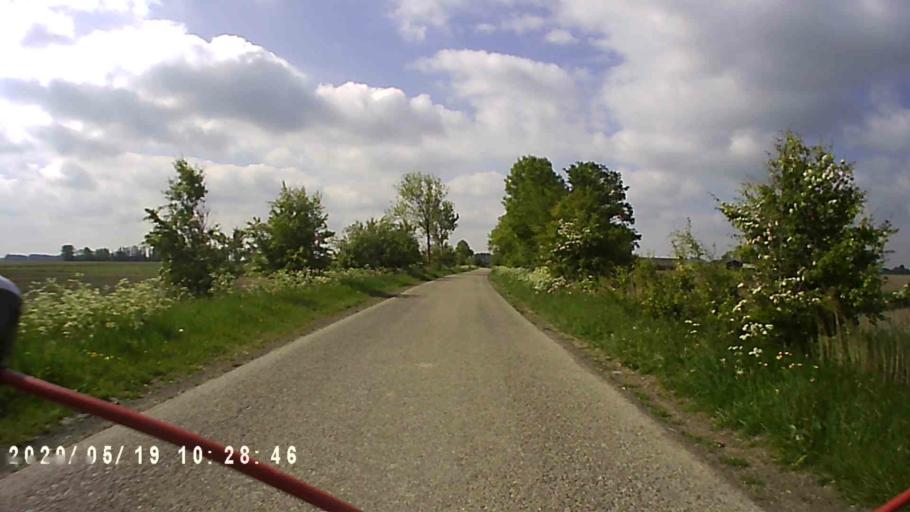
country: NL
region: Friesland
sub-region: Gemeente Kollumerland en Nieuwkruisland
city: Kollum
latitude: 53.3014
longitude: 6.1960
